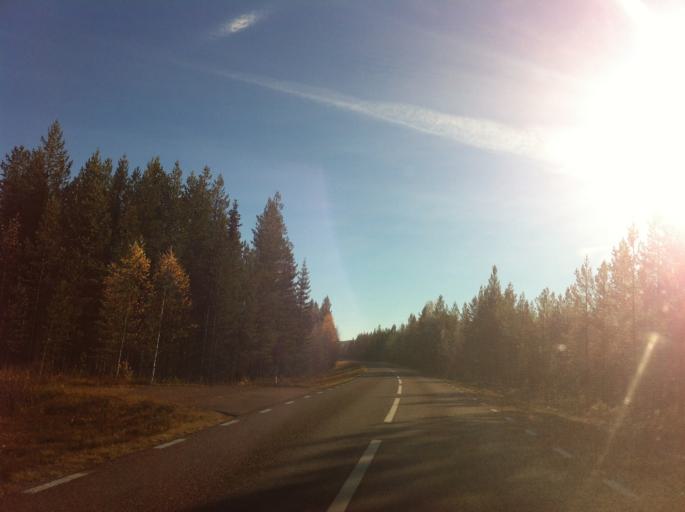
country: NO
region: Hedmark
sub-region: Trysil
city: Innbygda
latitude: 61.7097
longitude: 13.0113
